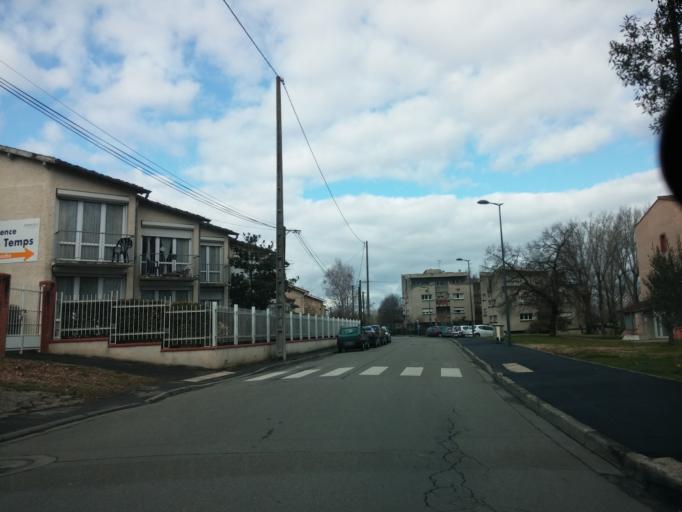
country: FR
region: Midi-Pyrenees
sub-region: Departement de la Haute-Garonne
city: Blagnac
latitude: 43.6363
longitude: 1.4002
